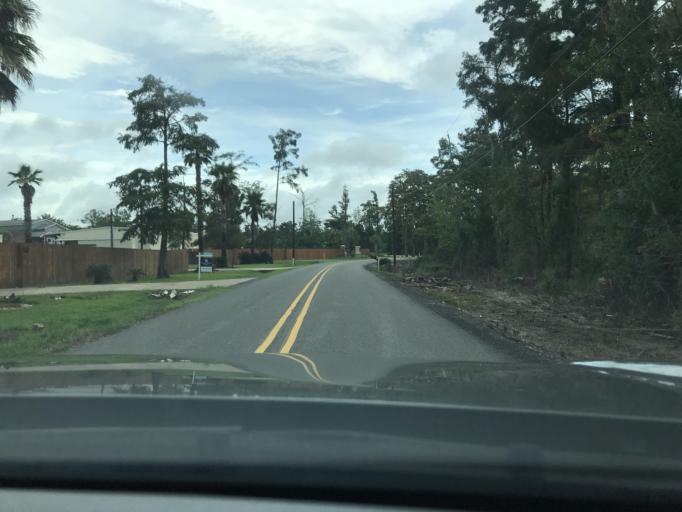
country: US
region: Louisiana
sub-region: Calcasieu Parish
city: Westlake
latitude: 30.2769
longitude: -93.2313
